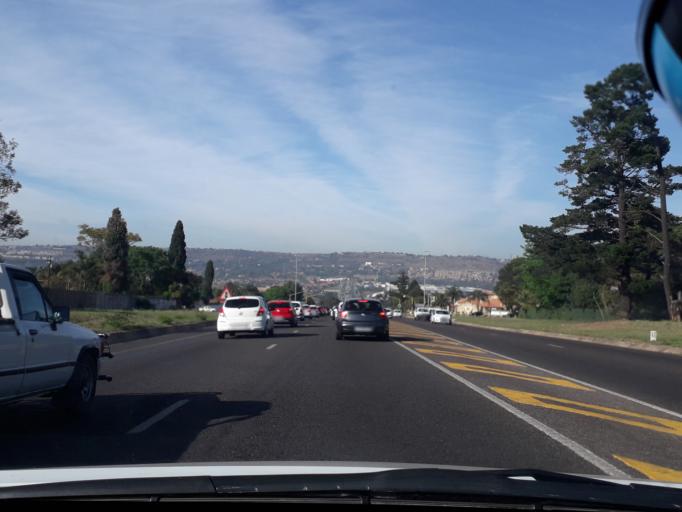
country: ZA
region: Gauteng
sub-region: City of Johannesburg Metropolitan Municipality
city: Roodepoort
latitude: -26.1111
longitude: 27.9201
